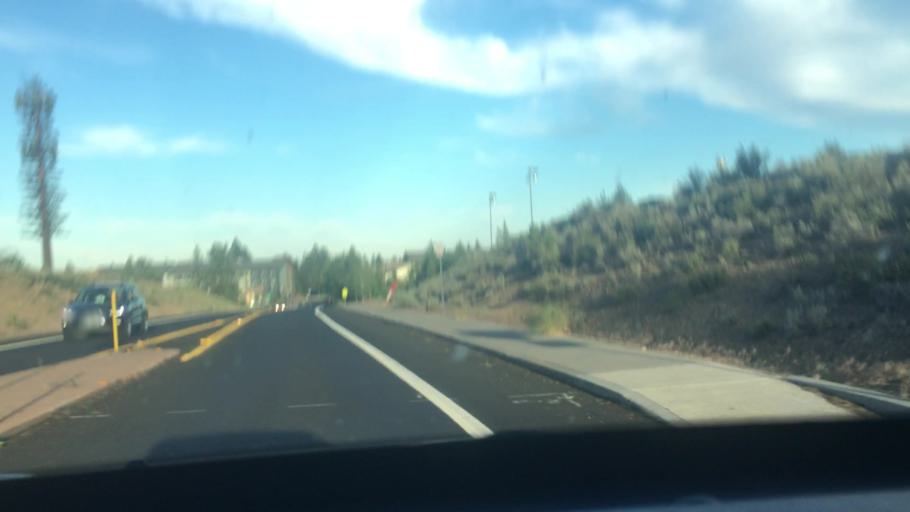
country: US
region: Oregon
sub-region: Deschutes County
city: Bend
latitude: 44.0405
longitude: -121.3406
